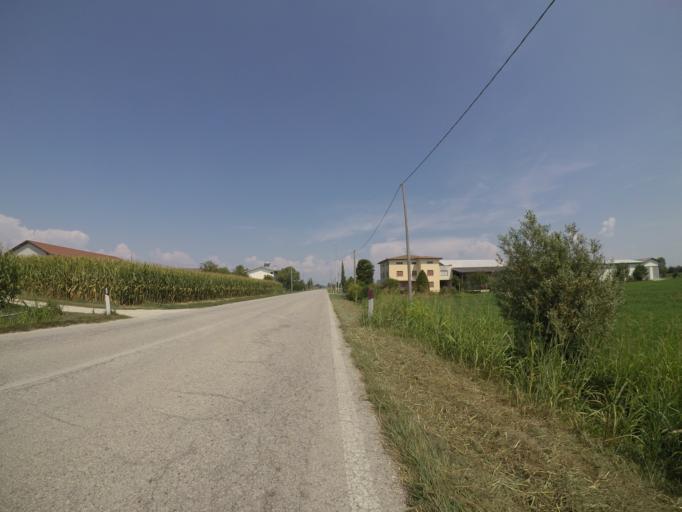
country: IT
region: Friuli Venezia Giulia
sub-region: Provincia di Udine
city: Pocenia
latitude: 45.8473
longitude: 13.1014
